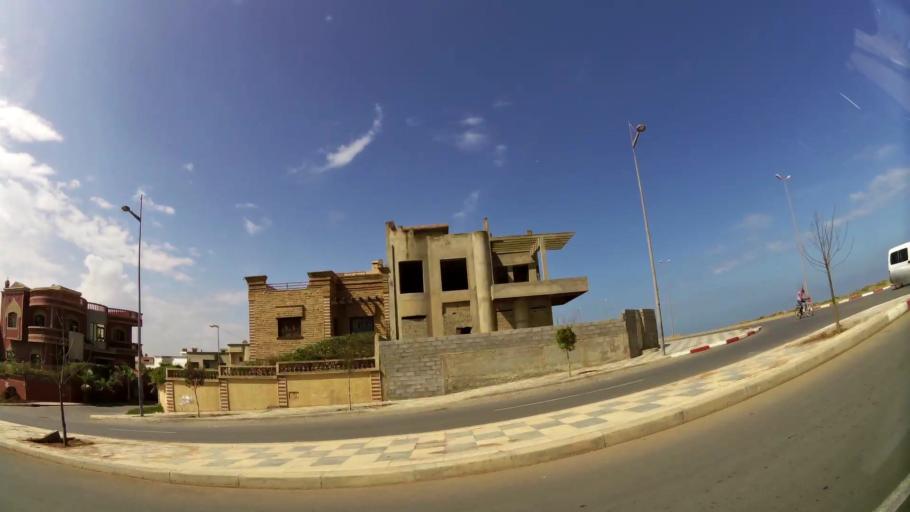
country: MA
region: Rabat-Sale-Zemmour-Zaer
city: Sale
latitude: 34.0742
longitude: -6.7989
